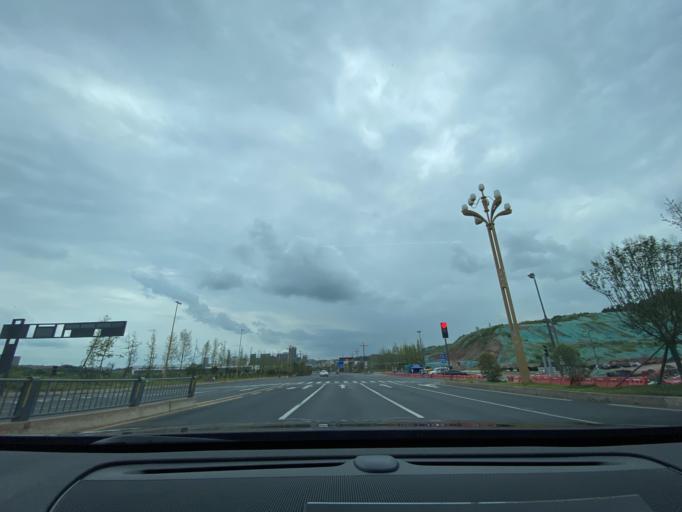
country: CN
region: Sichuan
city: Jiancheng
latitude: 30.4472
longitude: 104.4959
